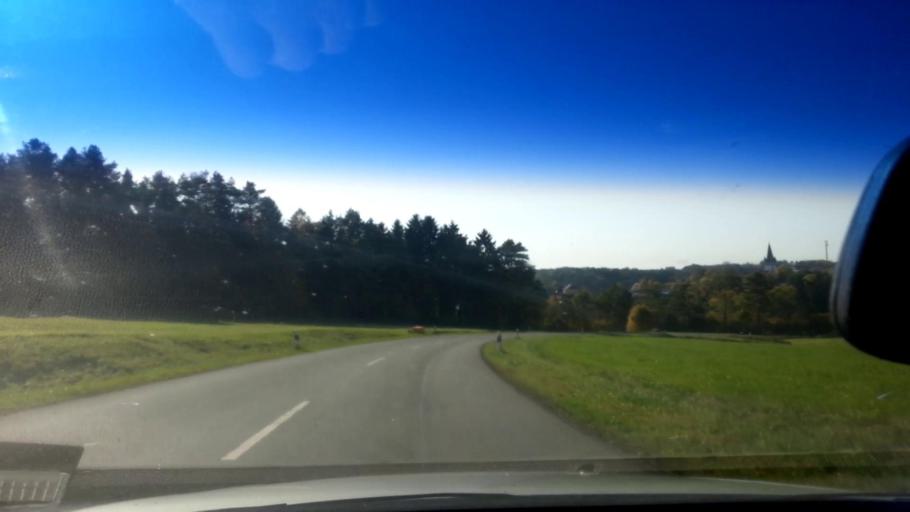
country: DE
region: Bavaria
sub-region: Upper Franconia
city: Wonsees
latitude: 49.9792
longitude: 11.3067
